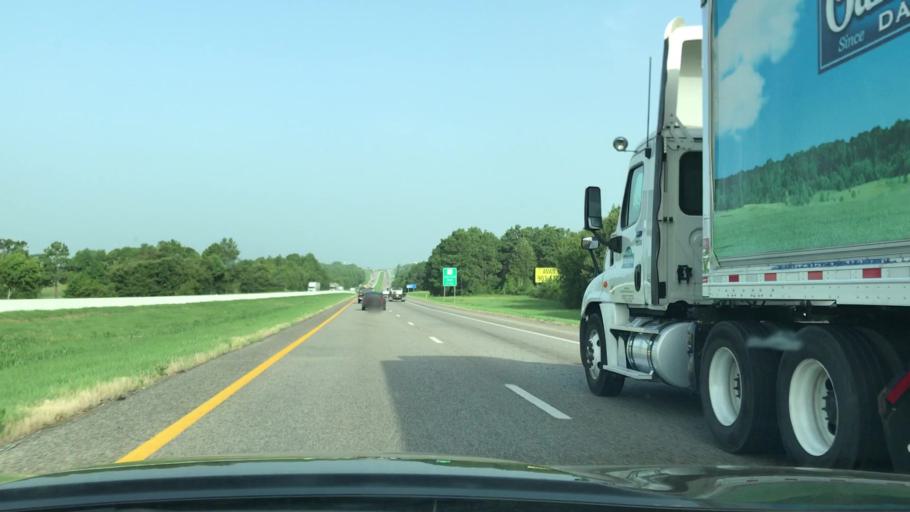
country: US
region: Texas
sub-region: Smith County
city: Hideaway
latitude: 32.4811
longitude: -95.5001
